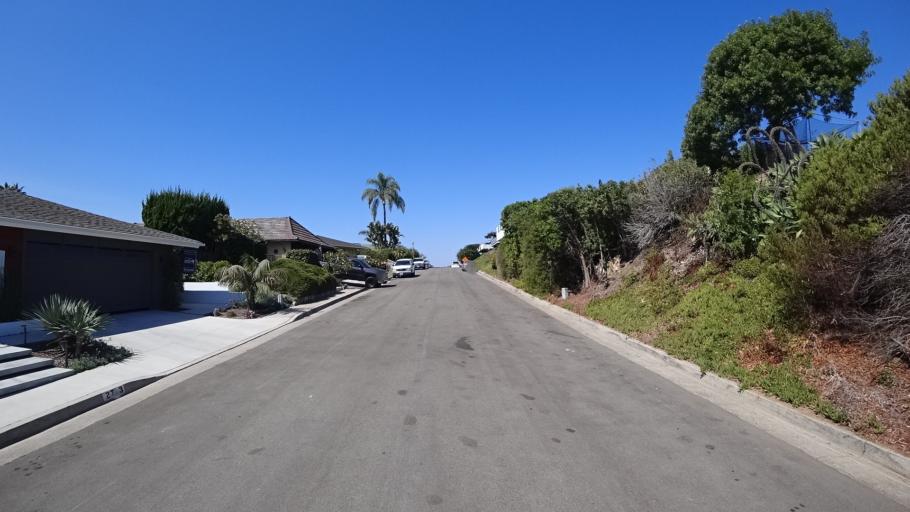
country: US
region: California
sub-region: Orange County
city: San Clemente
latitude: 33.4460
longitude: -117.6378
